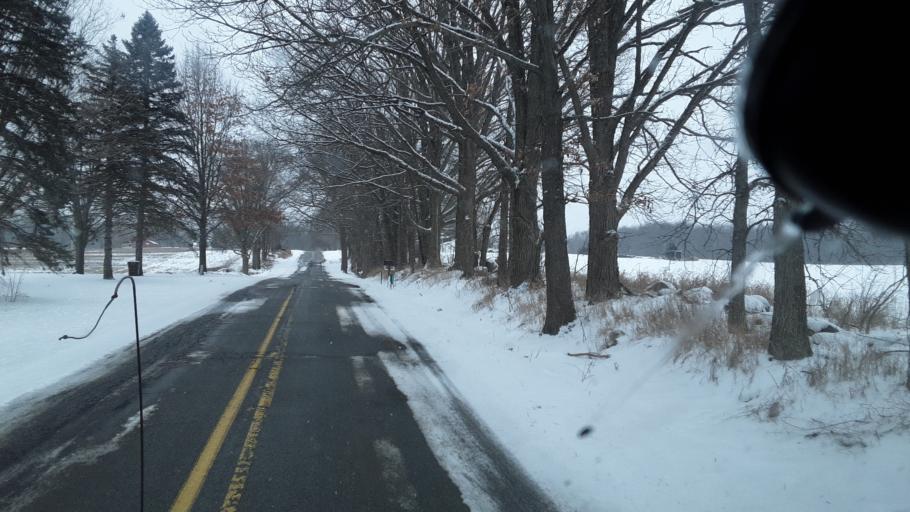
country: US
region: Michigan
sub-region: Ingham County
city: Leslie
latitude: 42.4292
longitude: -84.4775
